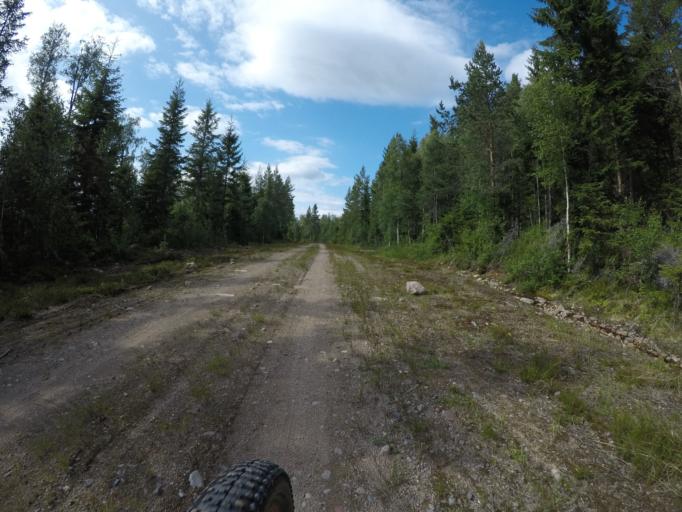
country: SE
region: Dalarna
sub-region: Ludvika Kommun
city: Abborrberget
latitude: 60.0570
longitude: 14.5687
